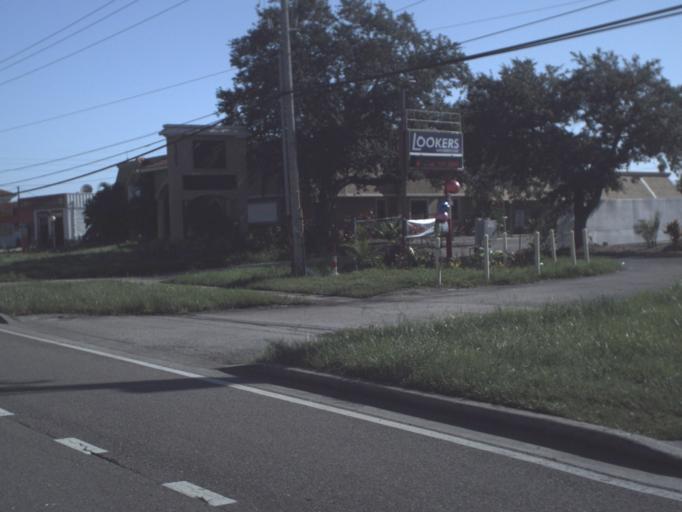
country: US
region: Florida
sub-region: Hillsborough County
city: Egypt Lake-Leto
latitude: 28.0235
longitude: -82.5049
